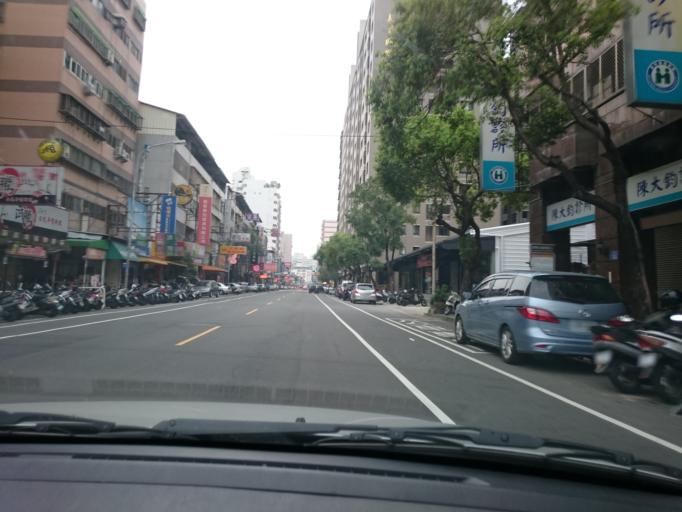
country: TW
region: Taiwan
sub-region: Taichung City
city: Taichung
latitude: 24.1441
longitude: 120.6372
